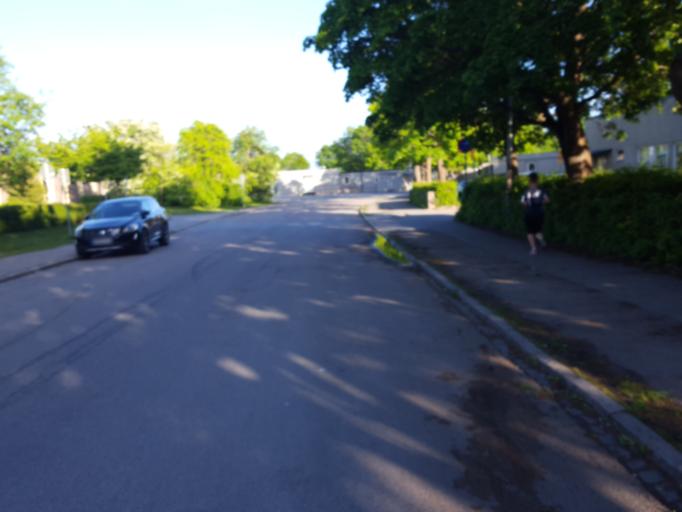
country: SE
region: Uppsala
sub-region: Uppsala Kommun
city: Uppsala
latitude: 59.8642
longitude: 17.6634
